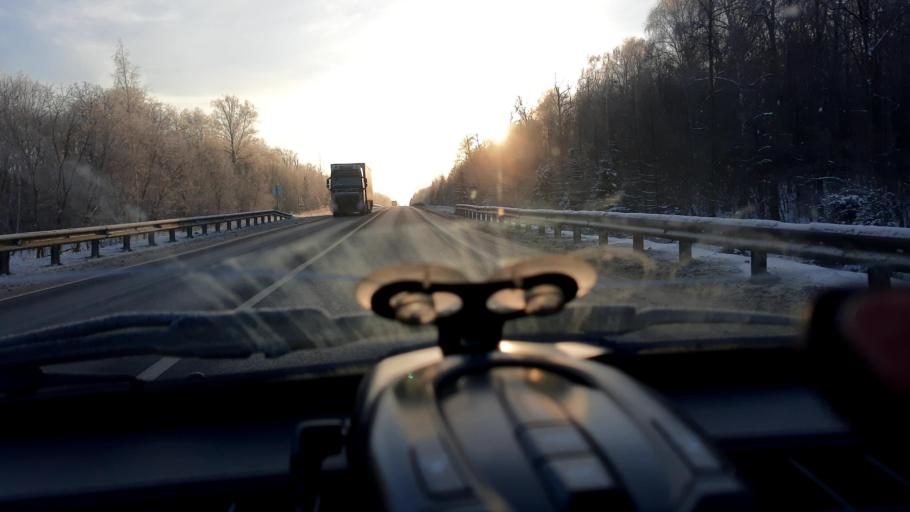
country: RU
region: Bashkortostan
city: Avdon
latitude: 54.8435
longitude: 55.7119
